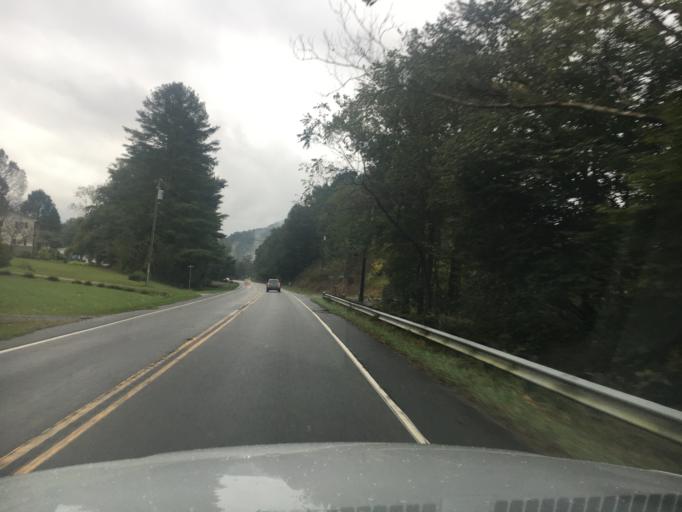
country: US
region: North Carolina
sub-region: Henderson County
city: Etowah
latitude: 35.3211
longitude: -82.5822
